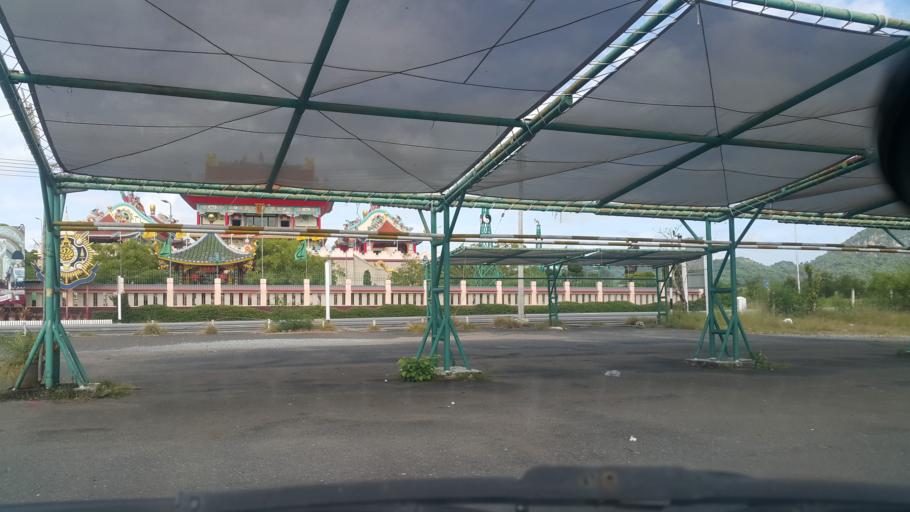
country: TH
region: Rayong
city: Ban Chang
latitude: 12.7881
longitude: 100.9541
